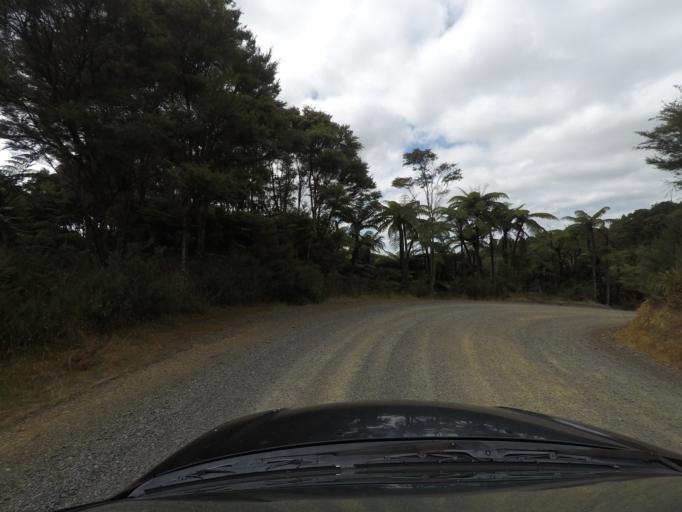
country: NZ
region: Northland
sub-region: Whangarei
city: Ruakaka
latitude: -35.9259
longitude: 174.3383
